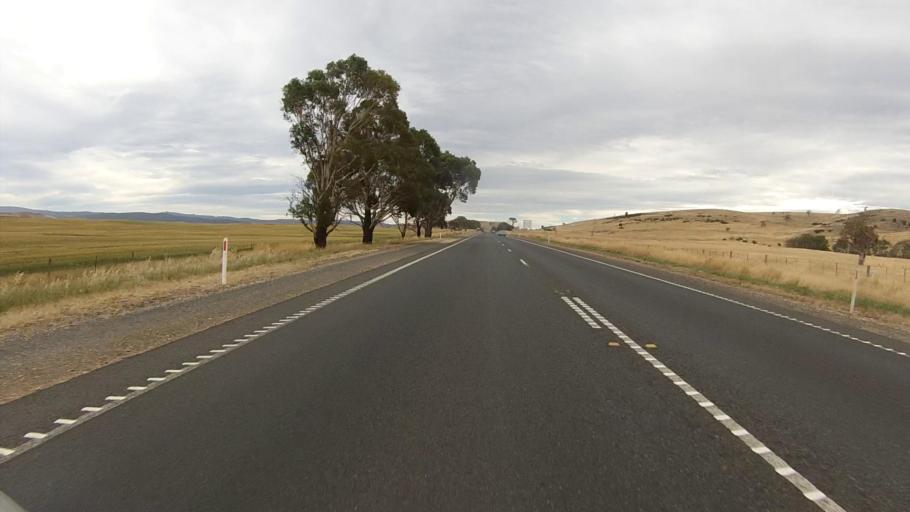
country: AU
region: Tasmania
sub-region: Brighton
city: Bridgewater
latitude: -42.3626
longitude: 147.3360
